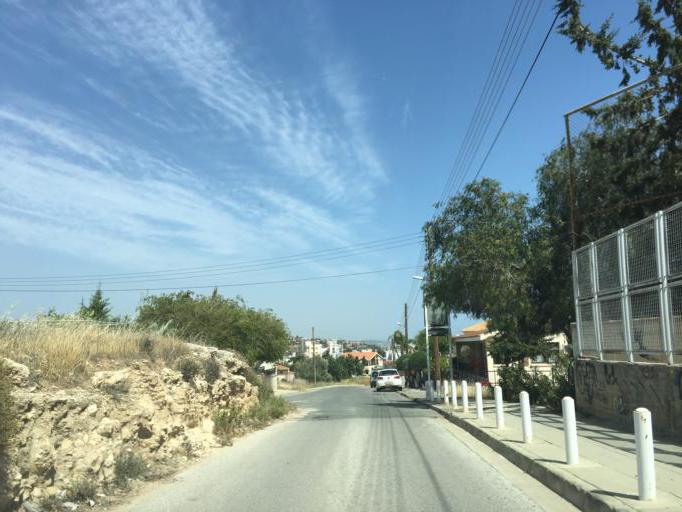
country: CY
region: Limassol
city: Mouttagiaka
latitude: 34.7044
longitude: 33.0795
